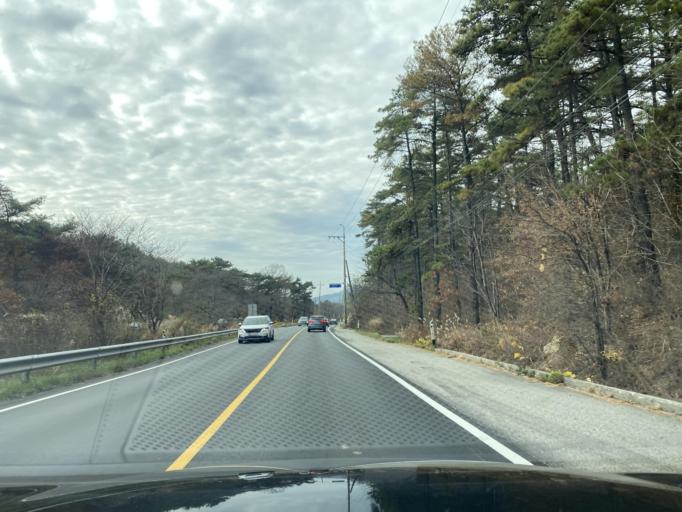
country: KR
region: Chungcheongnam-do
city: Hongsung
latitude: 36.6586
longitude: 126.6276
